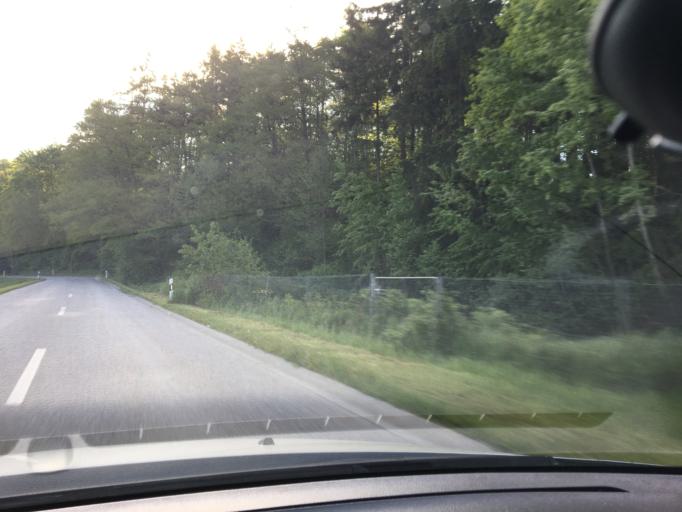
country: DE
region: Bavaria
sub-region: Lower Bavaria
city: Stallwang
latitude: 48.5303
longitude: 12.2332
